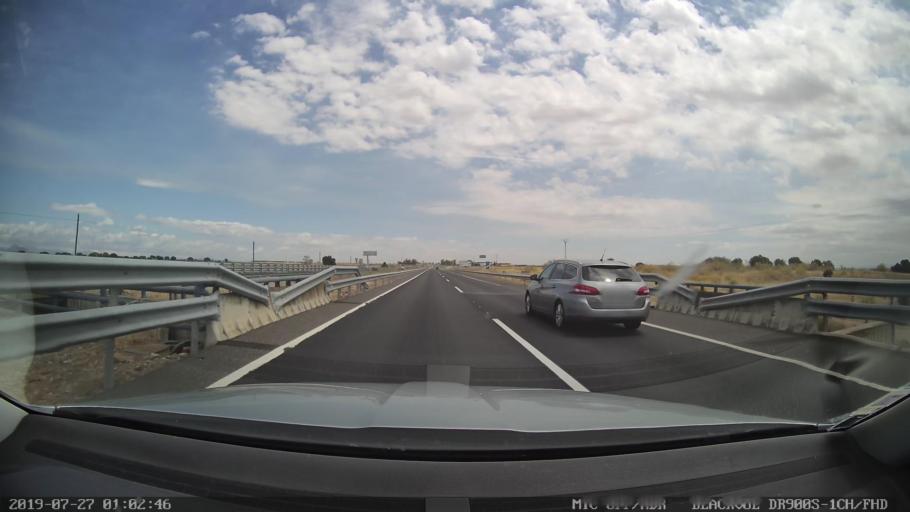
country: ES
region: Castille-La Mancha
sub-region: Province of Toledo
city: Cazalegas
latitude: 39.9870
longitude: -4.7103
